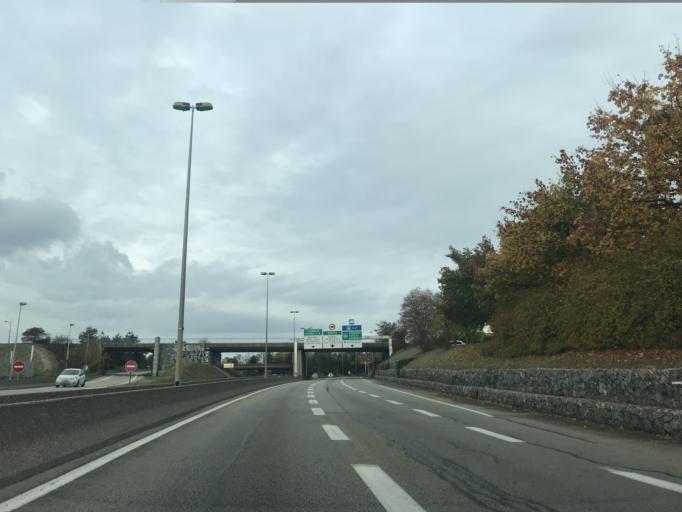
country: FR
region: Rhone-Alpes
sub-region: Departement de la Haute-Savoie
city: Metz-Tessy
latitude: 45.9324
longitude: 6.1192
